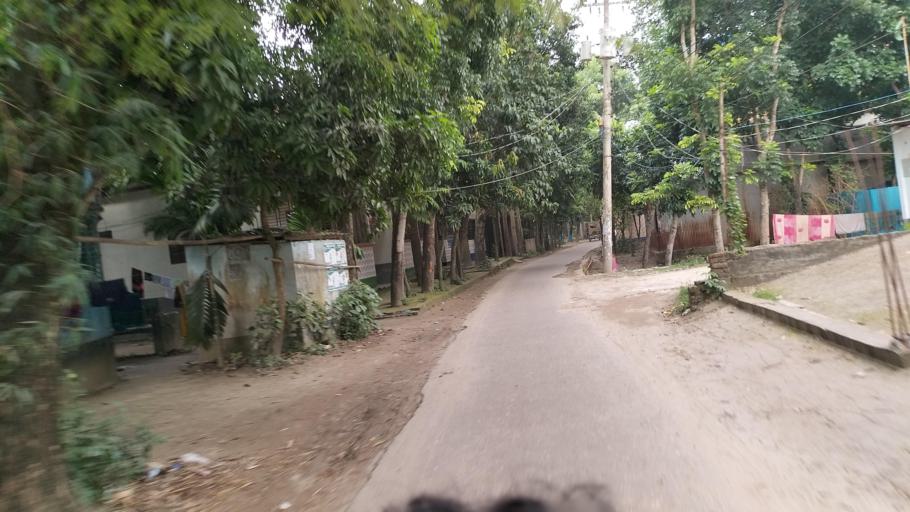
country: BD
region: Dhaka
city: Azimpur
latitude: 23.6841
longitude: 90.3107
